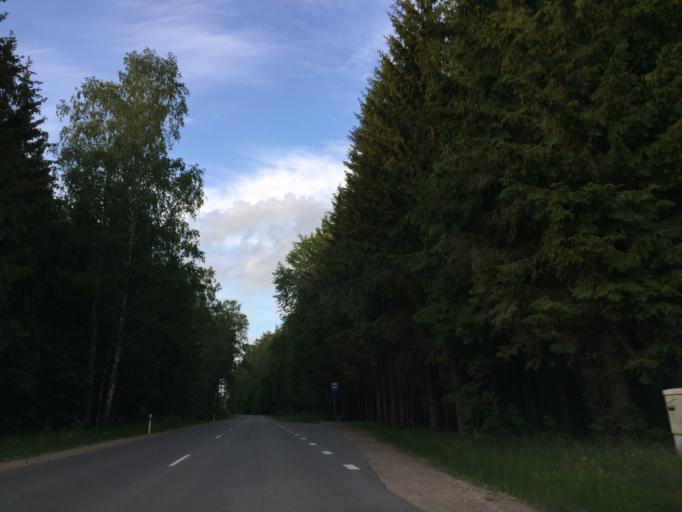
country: LV
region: Babite
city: Pinki
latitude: 56.9262
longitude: 23.8739
